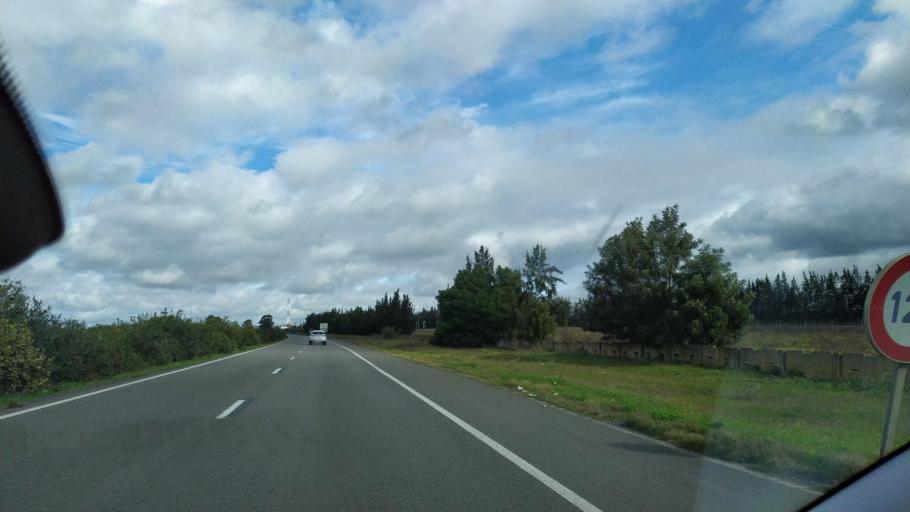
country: MA
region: Gharb-Chrarda-Beni Hssen
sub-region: Kenitra Province
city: Lalla Mimouna
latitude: 34.8814
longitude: -6.2116
